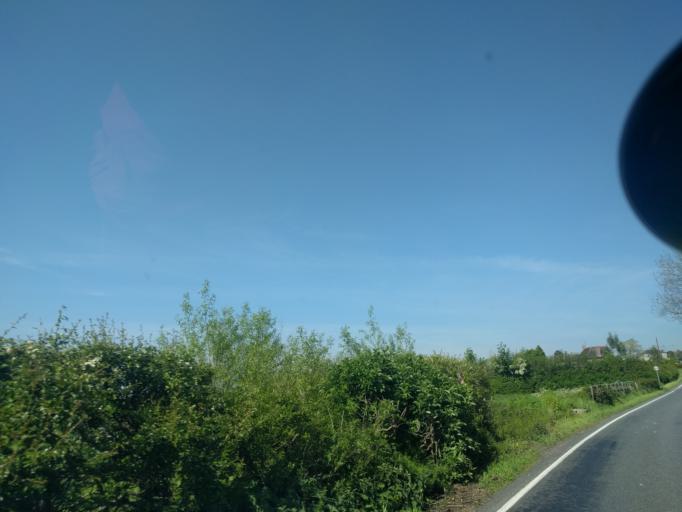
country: GB
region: England
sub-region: Somerset
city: Ilchester
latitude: 51.0288
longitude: -2.7081
